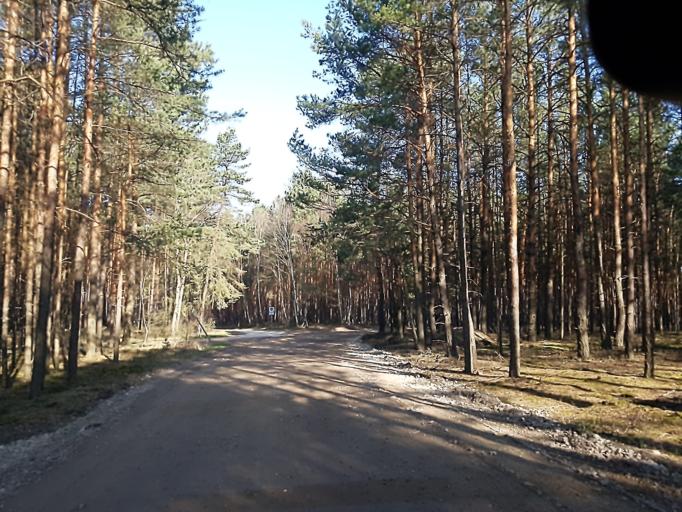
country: DE
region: Brandenburg
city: Tschernitz
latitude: 51.6609
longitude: 14.5641
